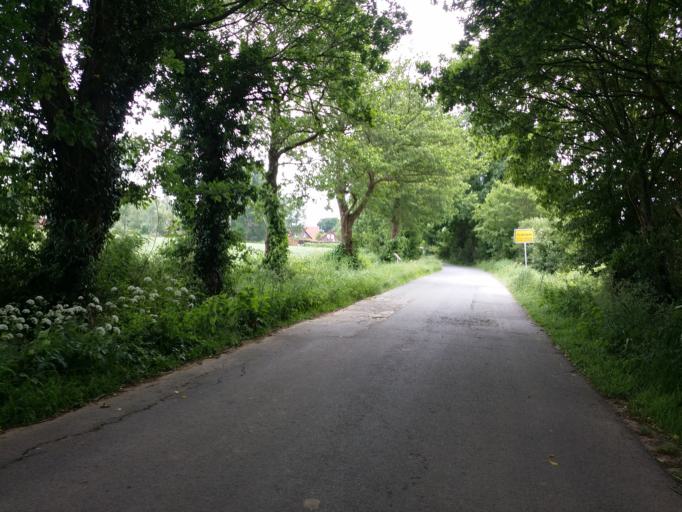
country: DE
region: Lower Saxony
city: Bockhorn
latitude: 53.3720
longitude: 7.9929
